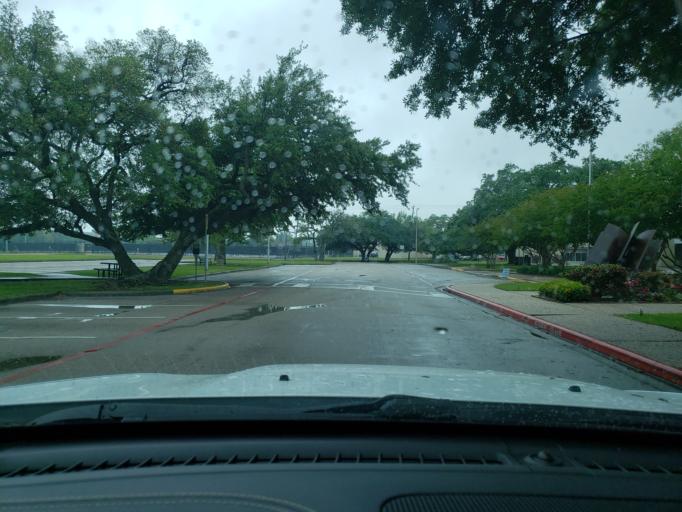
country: US
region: Texas
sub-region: Harris County
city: Baytown
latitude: 29.7369
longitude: -94.9792
